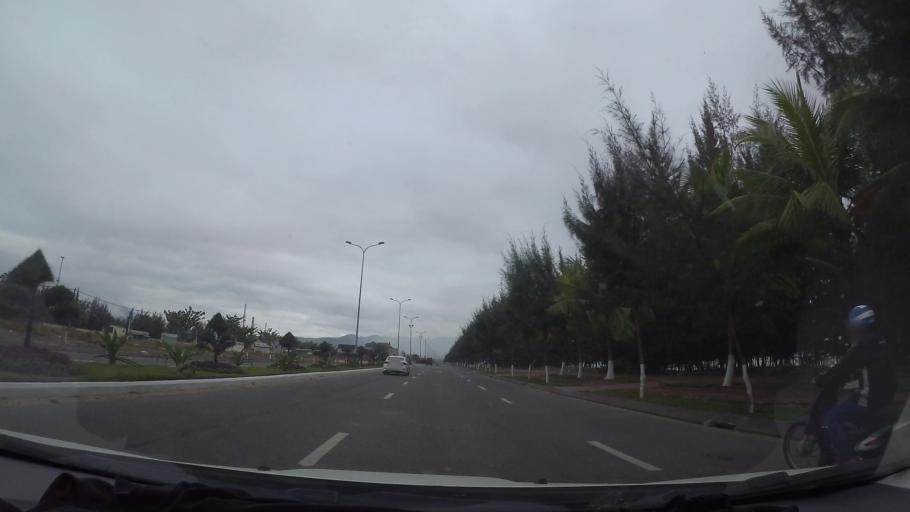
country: VN
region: Da Nang
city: Lien Chieu
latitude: 16.0982
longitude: 108.1427
